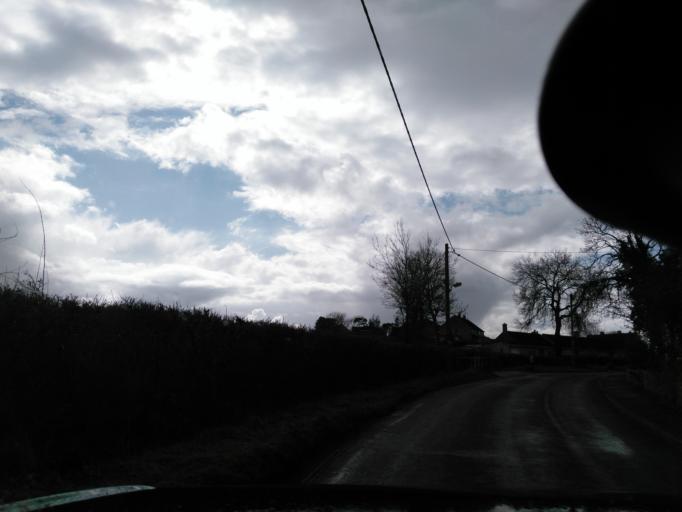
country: GB
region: England
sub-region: Wiltshire
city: Atworth
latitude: 51.3939
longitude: -2.1834
